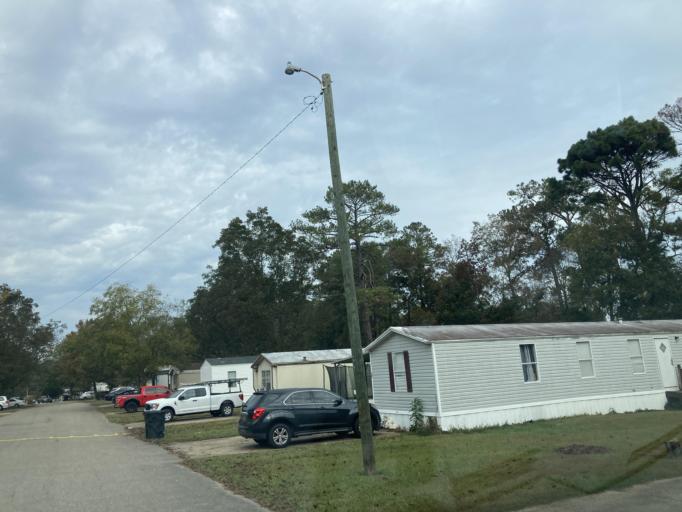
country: US
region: Mississippi
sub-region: Lamar County
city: West Hattiesburg
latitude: 31.3041
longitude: -89.3766
